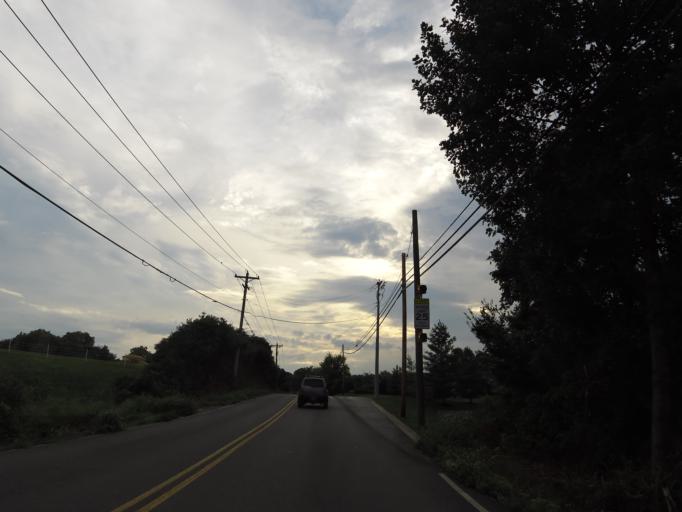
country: US
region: Tennessee
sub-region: Blount County
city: Maryville
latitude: 35.7354
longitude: -84.0209
